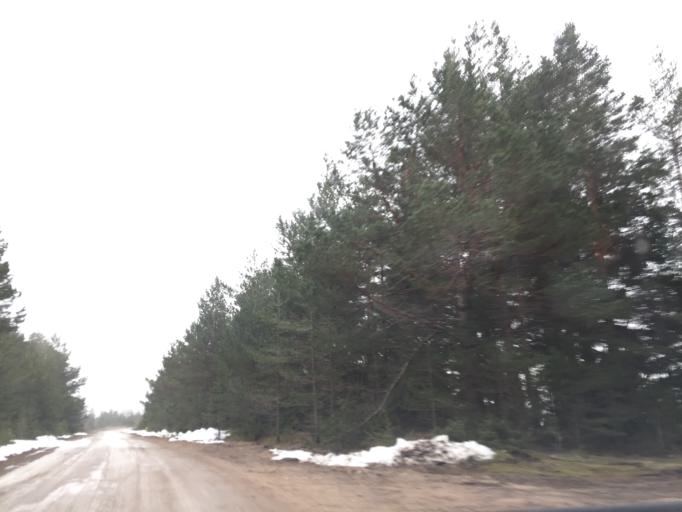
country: EE
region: Saare
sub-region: Kuressaare linn
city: Kuressaare
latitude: 58.4956
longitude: 21.9835
